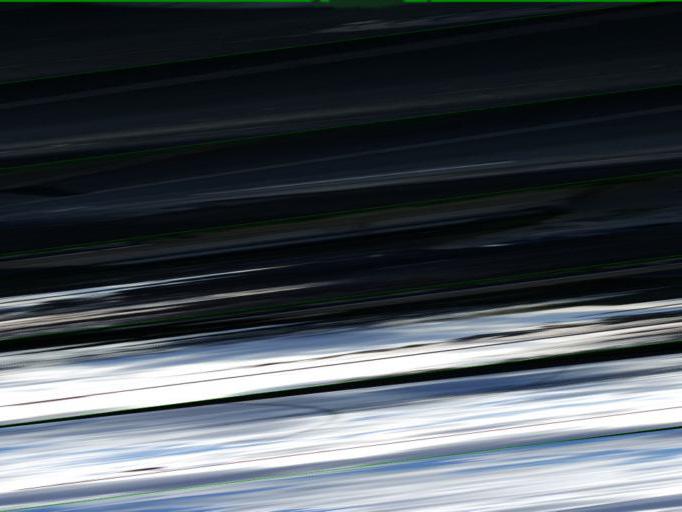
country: FR
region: Ile-de-France
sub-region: Departement du Val-d'Oise
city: Magny-en-Vexin
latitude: 49.1857
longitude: 1.8359
